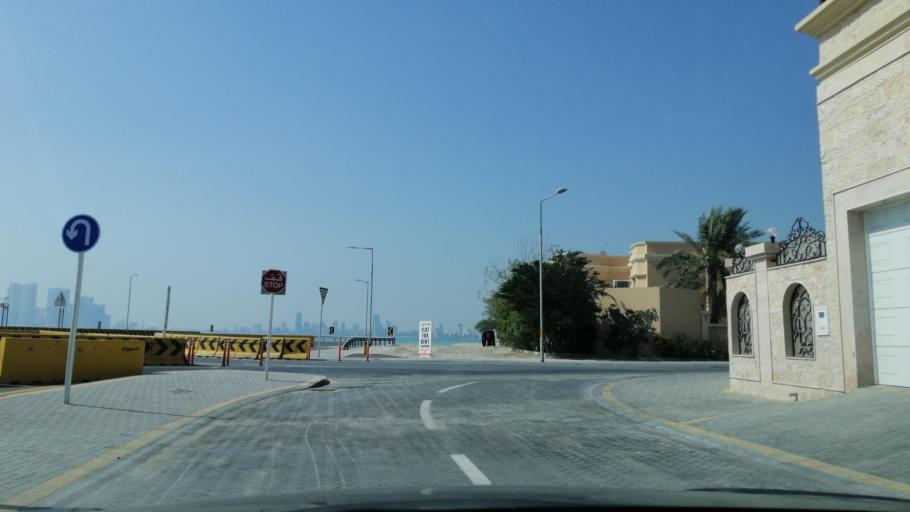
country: BH
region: Muharraq
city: Al Hadd
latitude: 26.2438
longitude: 50.6330
